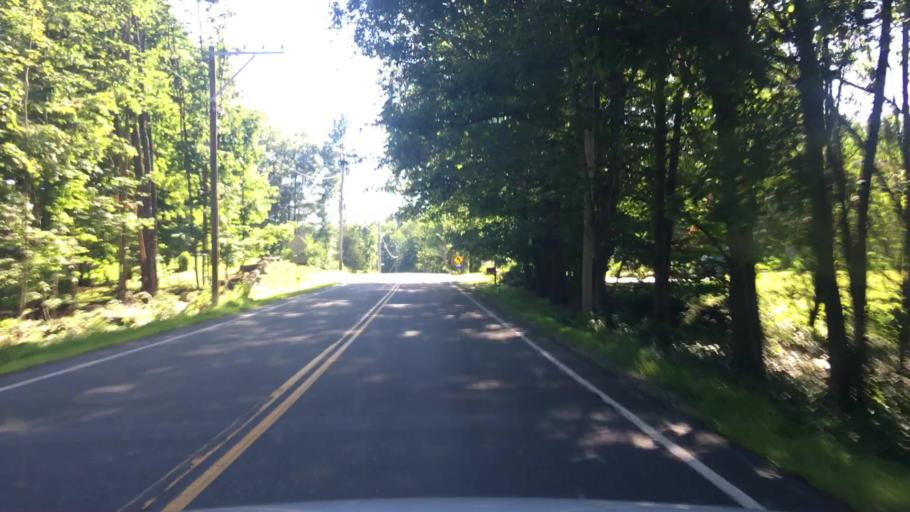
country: US
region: New Hampshire
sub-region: Rockingham County
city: Brentwood
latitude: 42.9893
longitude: -71.0508
